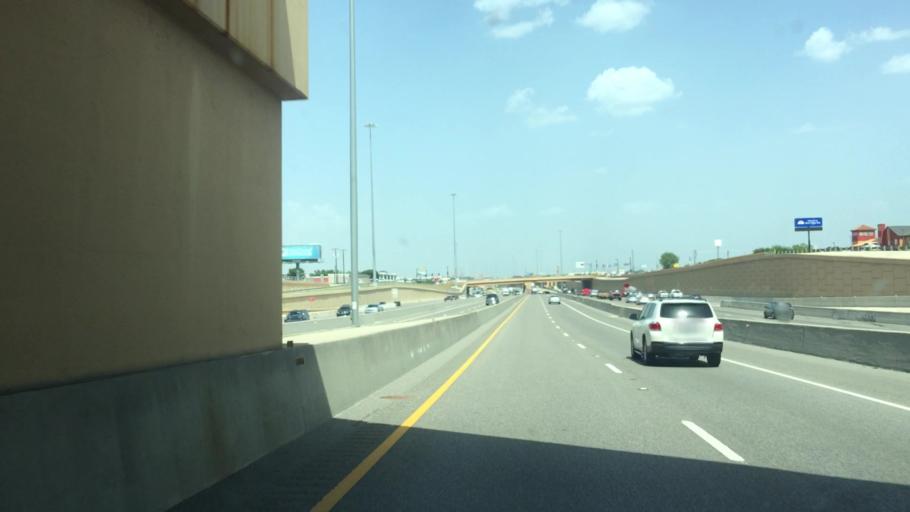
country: US
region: Texas
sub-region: Tarrant County
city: Watauga
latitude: 32.8396
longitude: -97.2689
